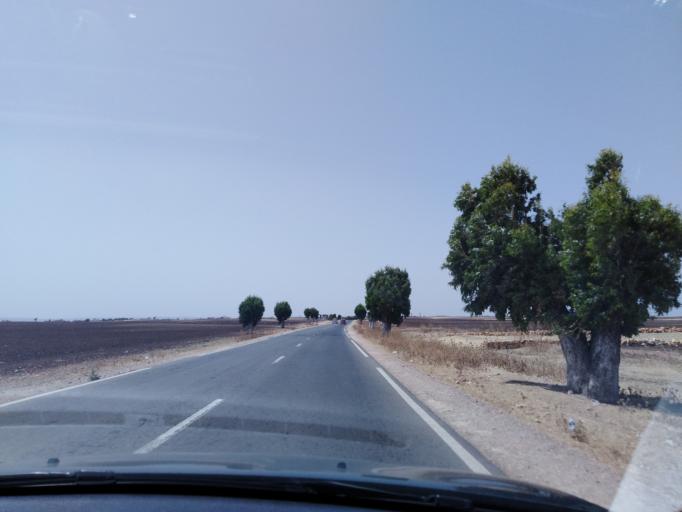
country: MA
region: Doukkala-Abda
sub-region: Safi
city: Youssoufia
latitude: 32.3903
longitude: -8.8224
